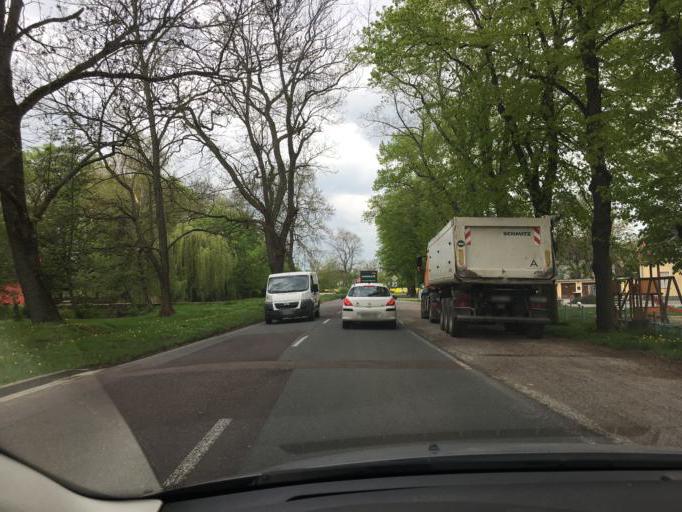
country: DE
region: Saxony-Anhalt
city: Giersleben
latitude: 51.7798
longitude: 11.5824
